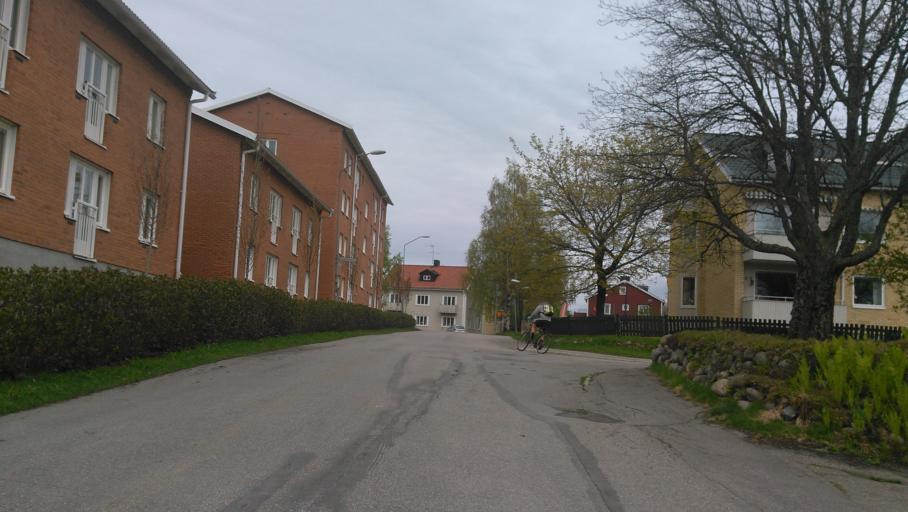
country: SE
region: Vaesterbotten
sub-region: Umea Kommun
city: Umea
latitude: 63.8188
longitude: 20.2850
